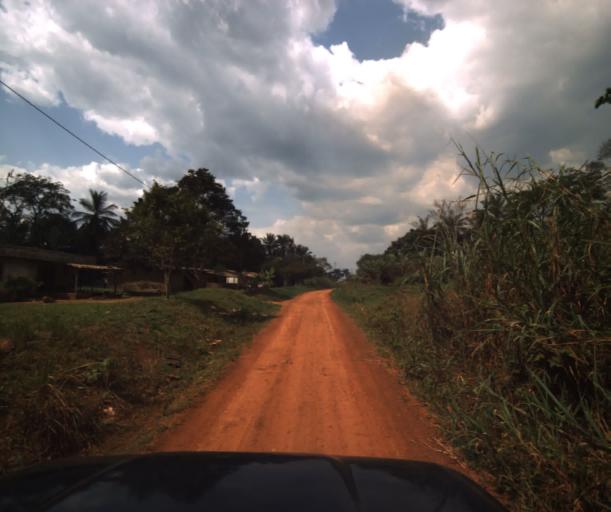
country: CM
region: Centre
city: Akono
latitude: 3.5915
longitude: 11.1617
